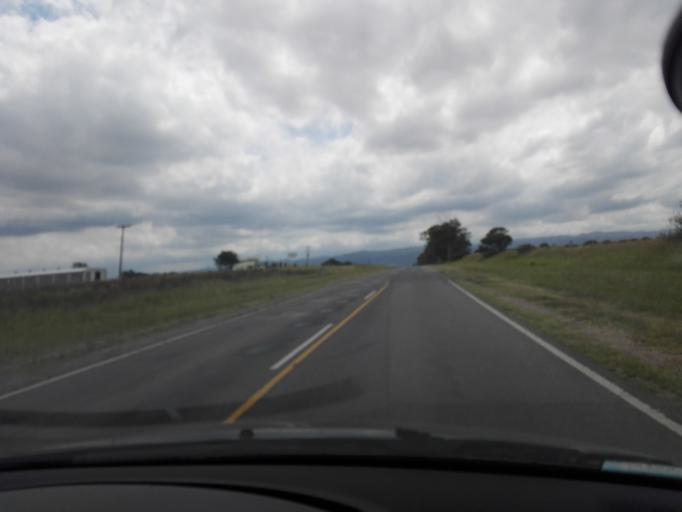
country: AR
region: Cordoba
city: Alta Gracia
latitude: -31.6581
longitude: -64.3770
